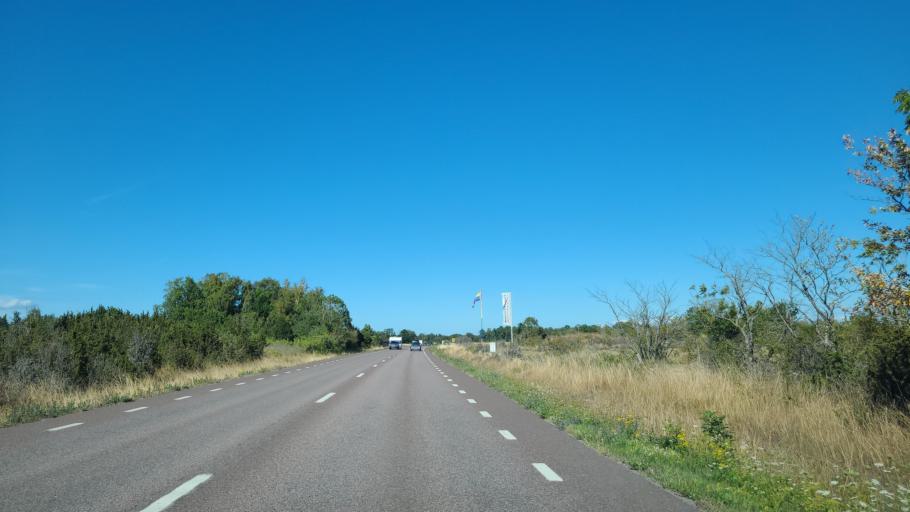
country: SE
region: Kalmar
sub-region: Borgholms Kommun
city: Borgholm
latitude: 57.0991
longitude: 16.9317
